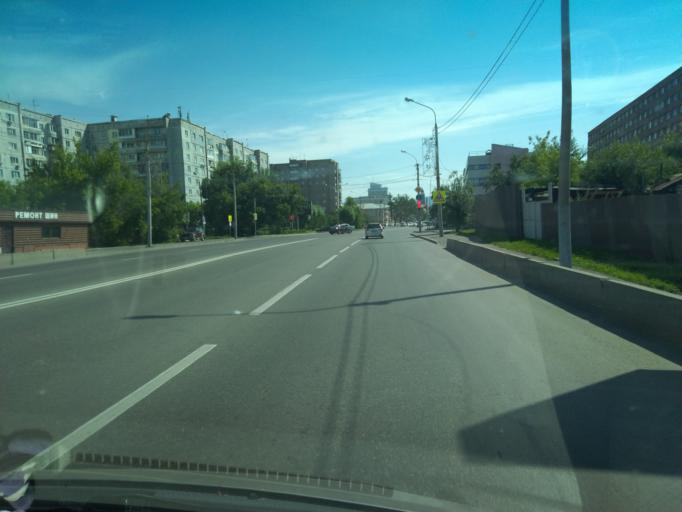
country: RU
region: Krasnoyarskiy
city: Krasnoyarsk
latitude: 56.0167
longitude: 92.8702
